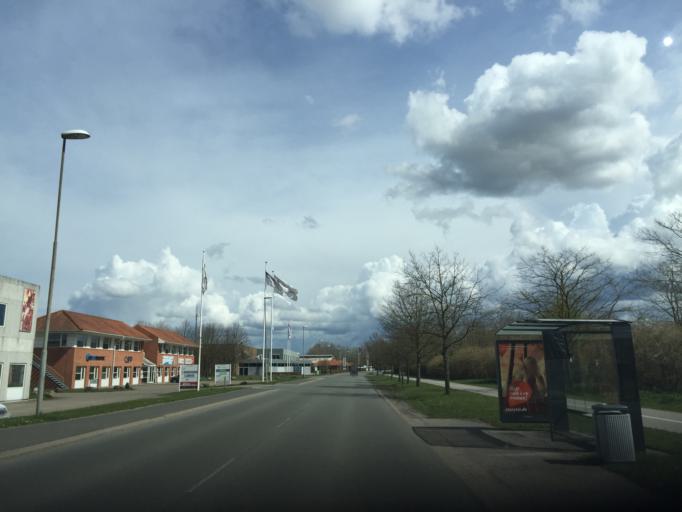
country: DK
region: South Denmark
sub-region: Odense Kommune
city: Odense
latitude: 55.3689
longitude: 10.3960
